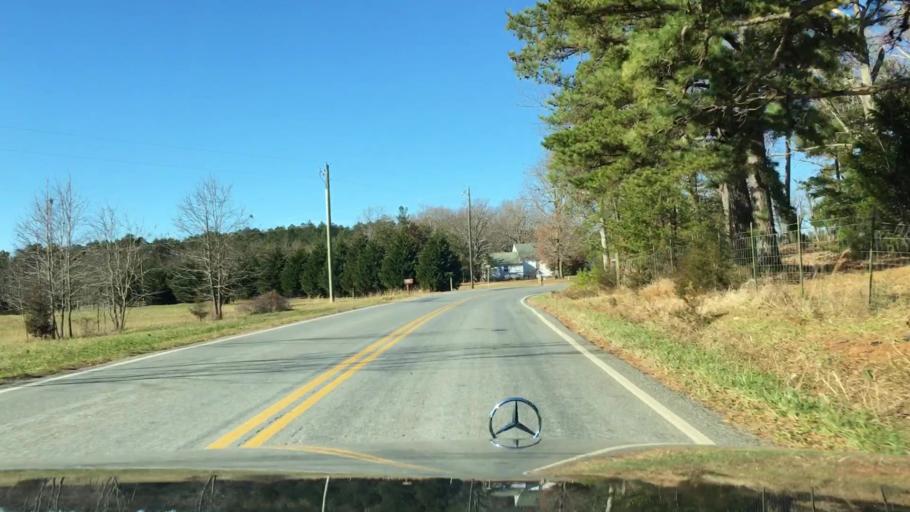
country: US
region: Virginia
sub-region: Pittsylvania County
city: Motley
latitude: 37.1632
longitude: -79.4028
